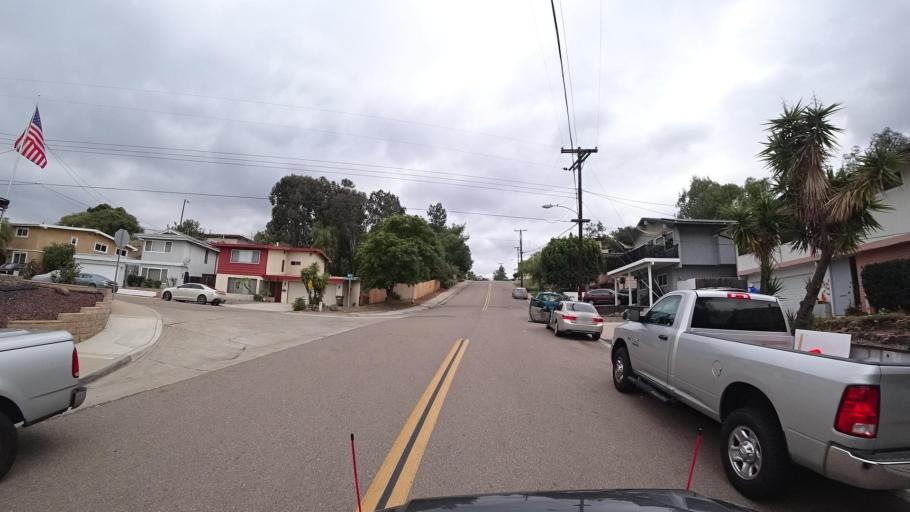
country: US
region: California
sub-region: San Diego County
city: Spring Valley
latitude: 32.7492
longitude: -117.0108
